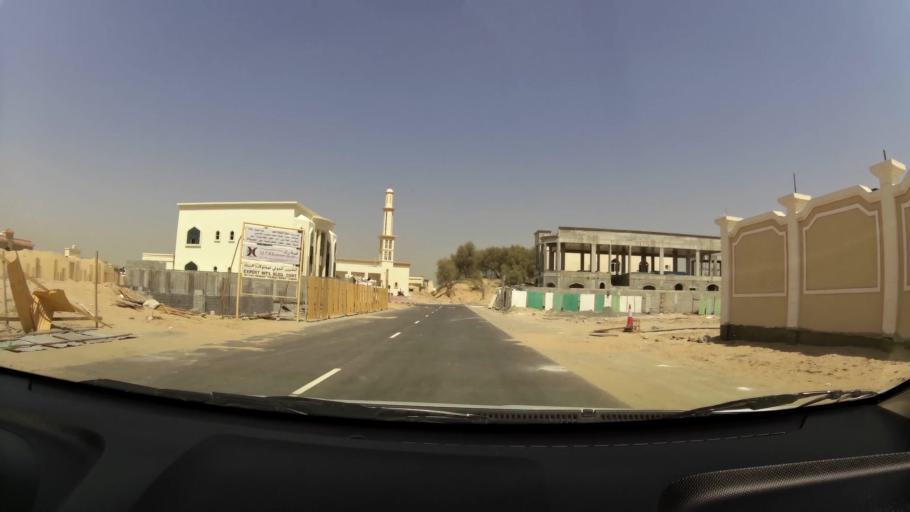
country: AE
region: Ajman
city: Ajman
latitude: 25.4057
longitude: 55.5321
